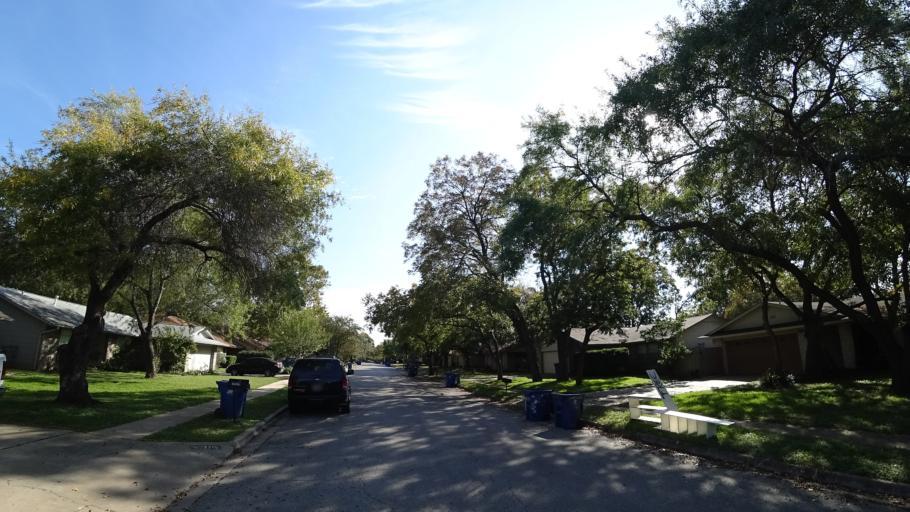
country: US
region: Texas
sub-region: Williamson County
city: Anderson Mill
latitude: 30.4576
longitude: -97.8018
